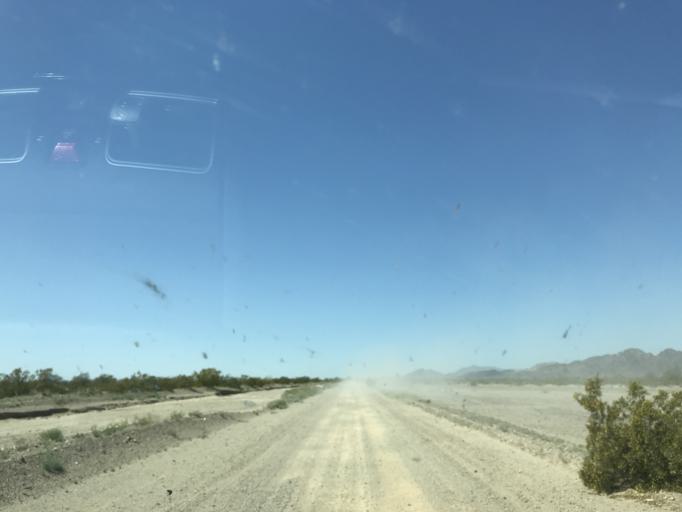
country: US
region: California
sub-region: Riverside County
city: Mesa Verde
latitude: 33.4884
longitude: -114.8985
